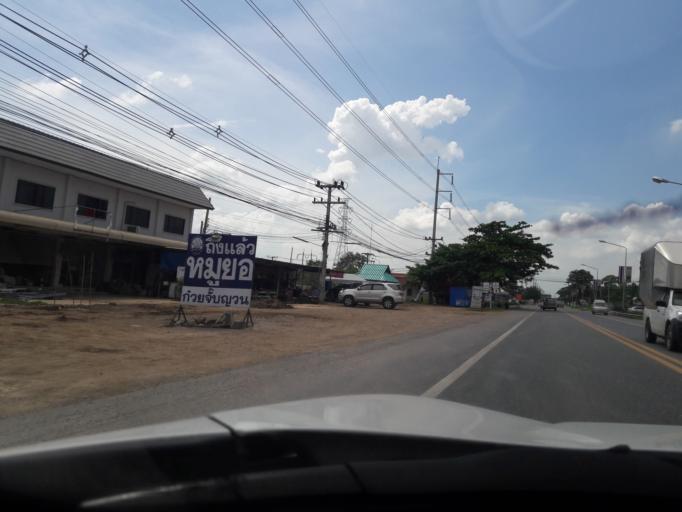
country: TH
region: Phra Nakhon Si Ayutthaya
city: Maha Rat
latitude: 14.5789
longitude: 100.5121
